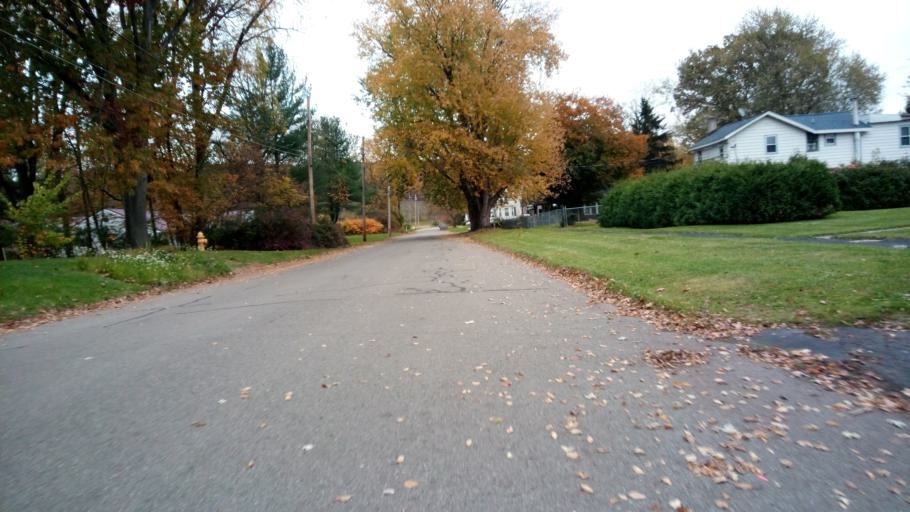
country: US
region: New York
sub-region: Chemung County
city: Elmira
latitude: 42.0822
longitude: -76.7876
